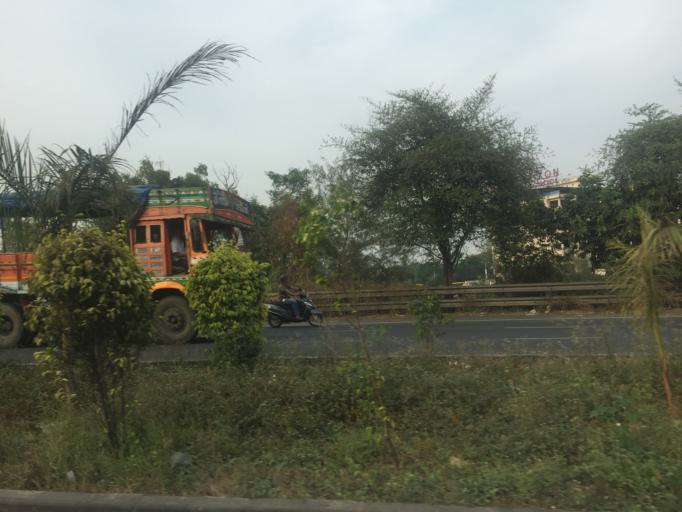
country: IN
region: Maharashtra
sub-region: Thane
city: Airoli
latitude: 19.1498
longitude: 72.9859
